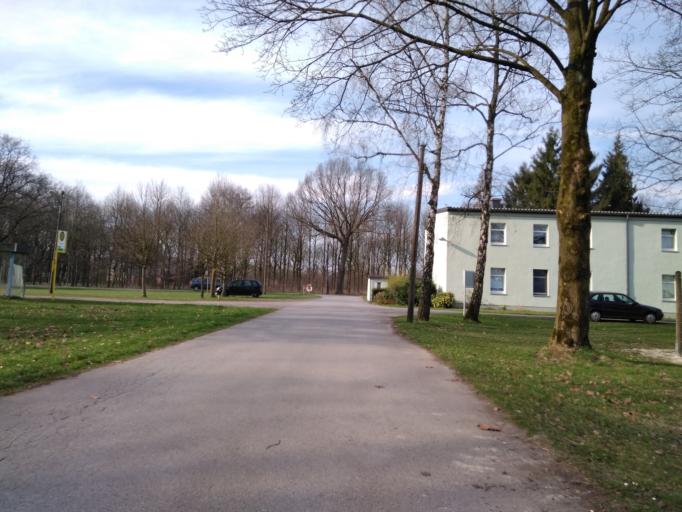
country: DE
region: North Rhine-Westphalia
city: Dorsten
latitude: 51.6358
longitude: 6.9727
